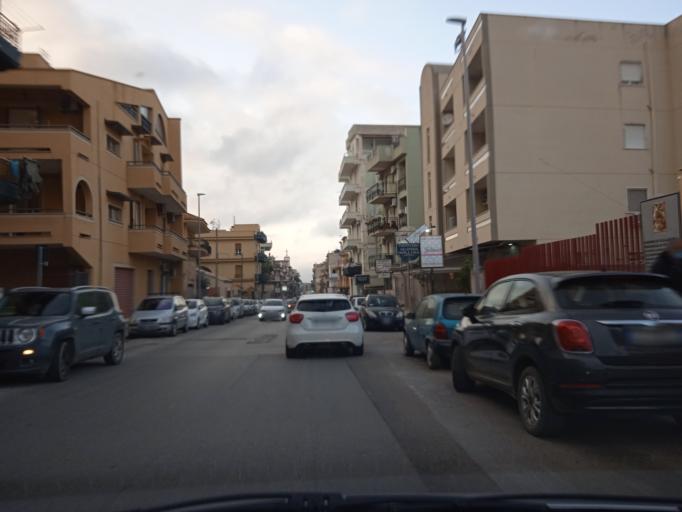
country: IT
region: Sicily
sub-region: Palermo
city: Villabate
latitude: 38.0780
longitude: 13.4383
